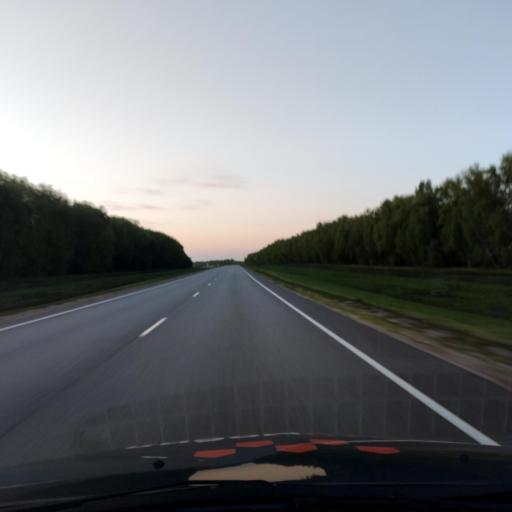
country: RU
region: Orjol
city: Zmiyevka
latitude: 52.6494
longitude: 36.5274
